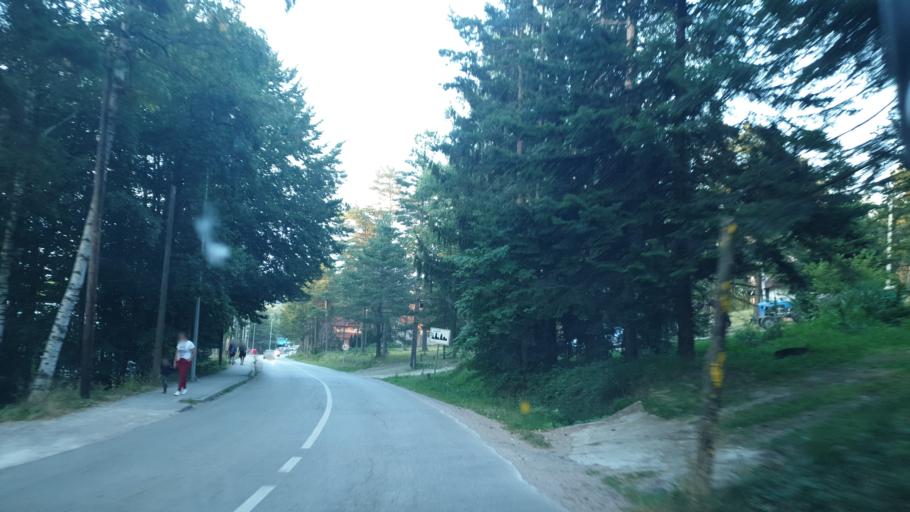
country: RS
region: Central Serbia
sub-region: Zlatiborski Okrug
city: Kosjeric
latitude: 44.0992
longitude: 19.9877
